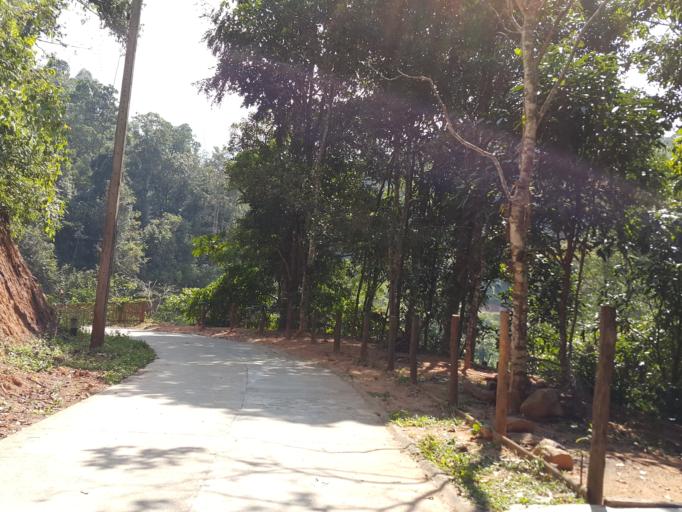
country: TH
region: Lampang
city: Wang Nuea
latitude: 19.0664
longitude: 99.3584
